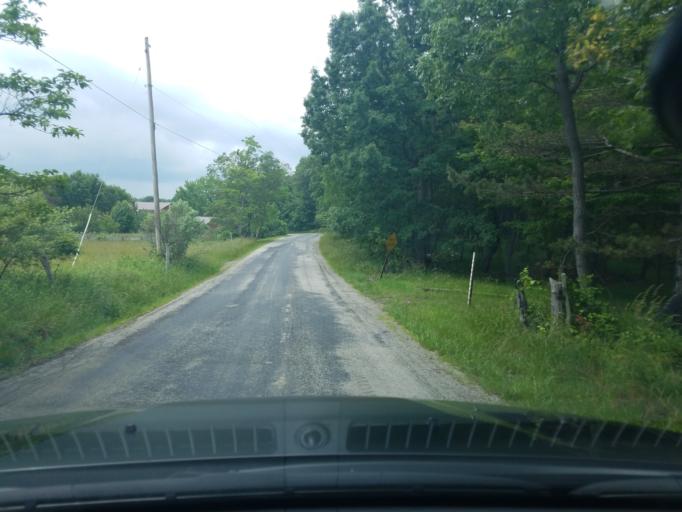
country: US
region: Pennsylvania
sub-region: Fayette County
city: Bear Rocks
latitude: 40.1816
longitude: -79.4045
